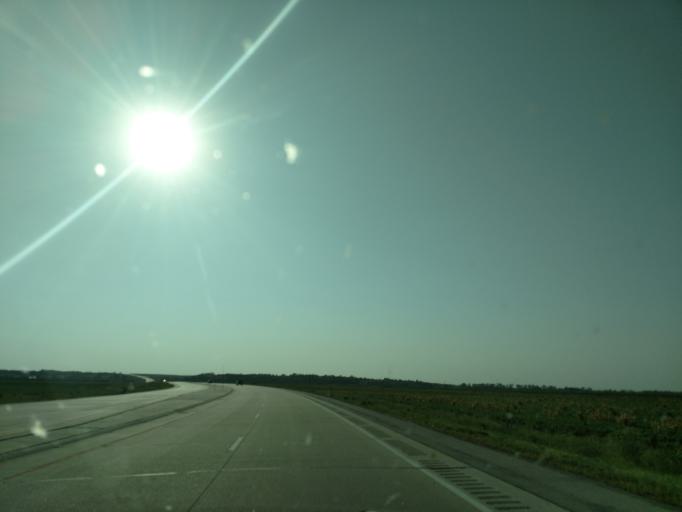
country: US
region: Nebraska
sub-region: Sarpy County
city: Offutt Air Force Base
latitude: 41.0777
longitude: -95.8932
